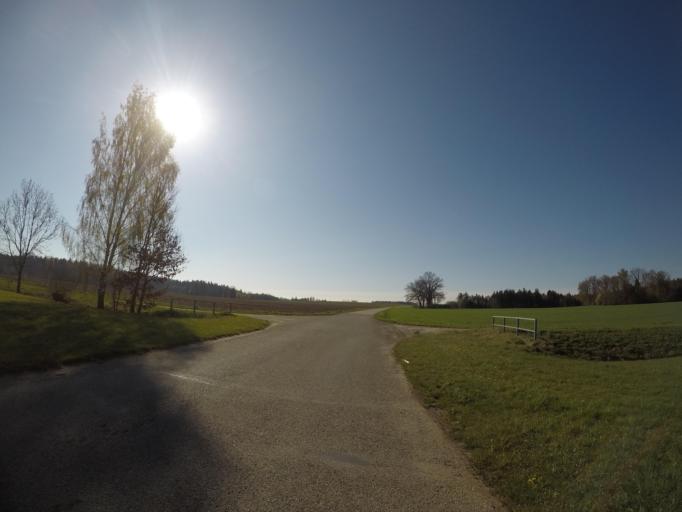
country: DE
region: Baden-Wuerttemberg
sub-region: Tuebingen Region
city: Altshausen
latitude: 47.9209
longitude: 9.5221
